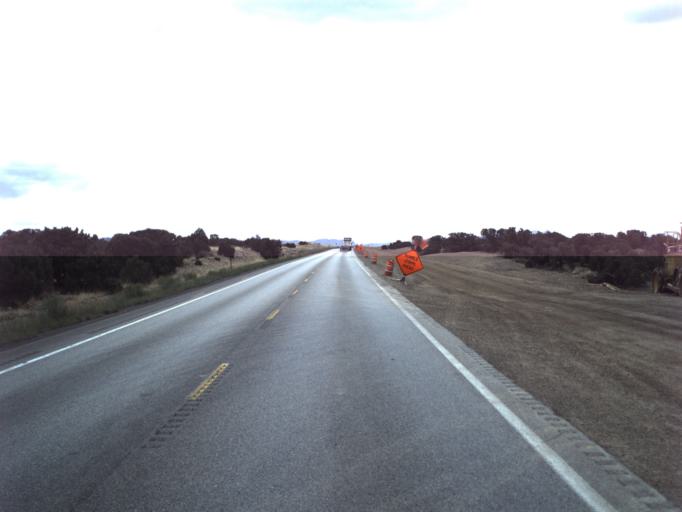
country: US
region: Utah
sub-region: Carbon County
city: East Carbon City
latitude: 39.4207
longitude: -110.4413
